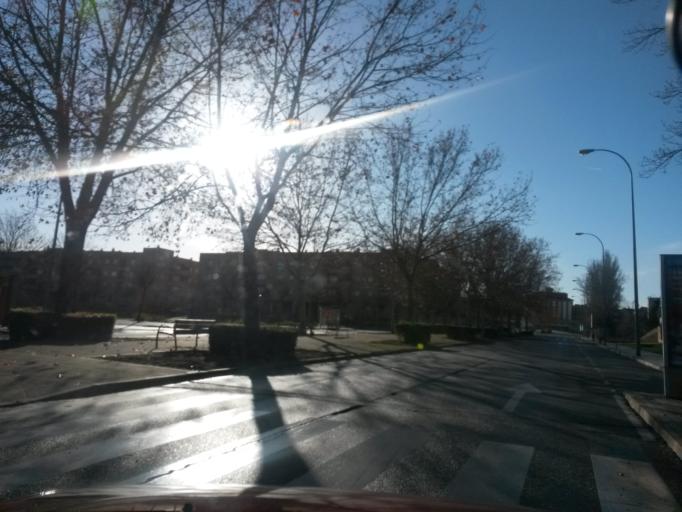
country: ES
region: Castille and Leon
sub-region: Provincia de Salamanca
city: Salamanca
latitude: 40.9578
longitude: -5.6860
